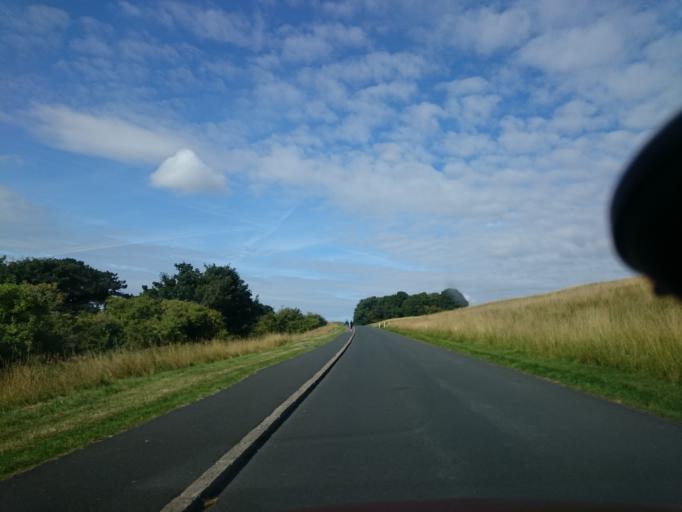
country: IE
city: Greenhills
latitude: 53.3478
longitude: -6.3157
